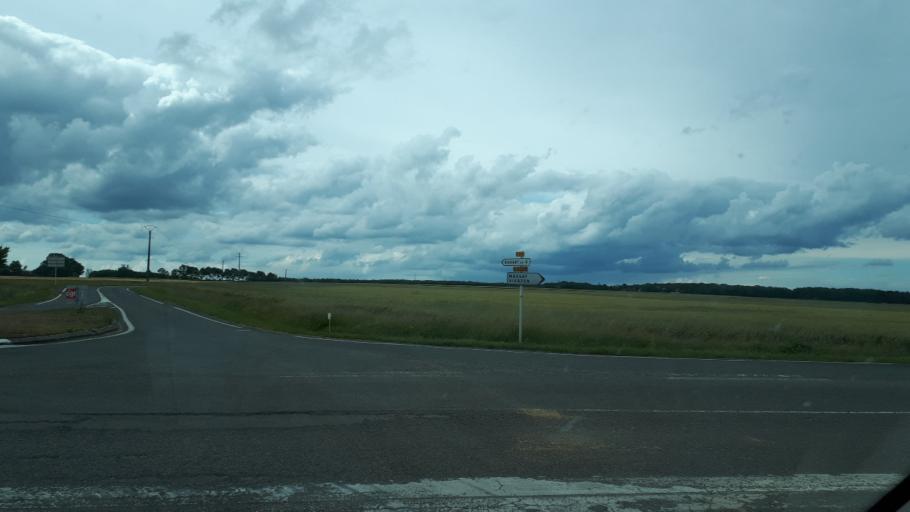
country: FR
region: Centre
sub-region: Departement du Cher
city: Gracay
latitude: 47.1220
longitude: 1.9217
